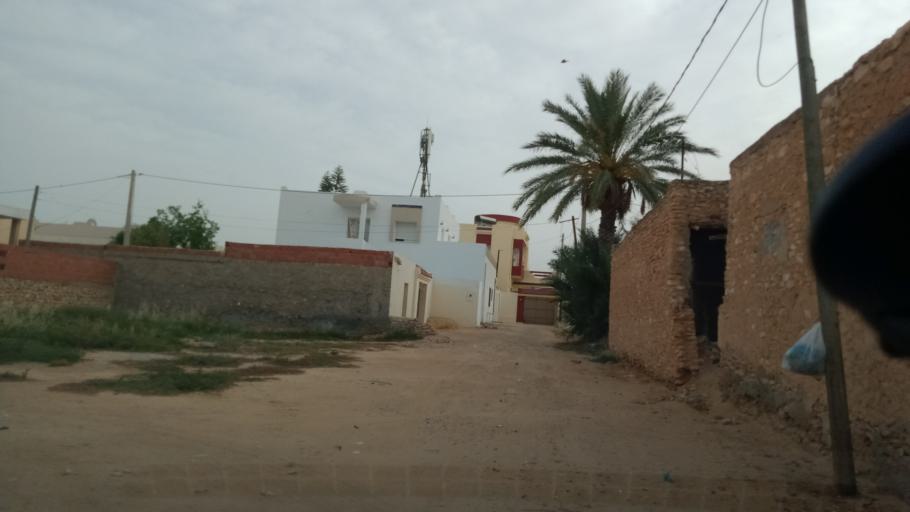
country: TN
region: Safaqis
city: Al Qarmadah
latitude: 34.7886
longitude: 10.7666
